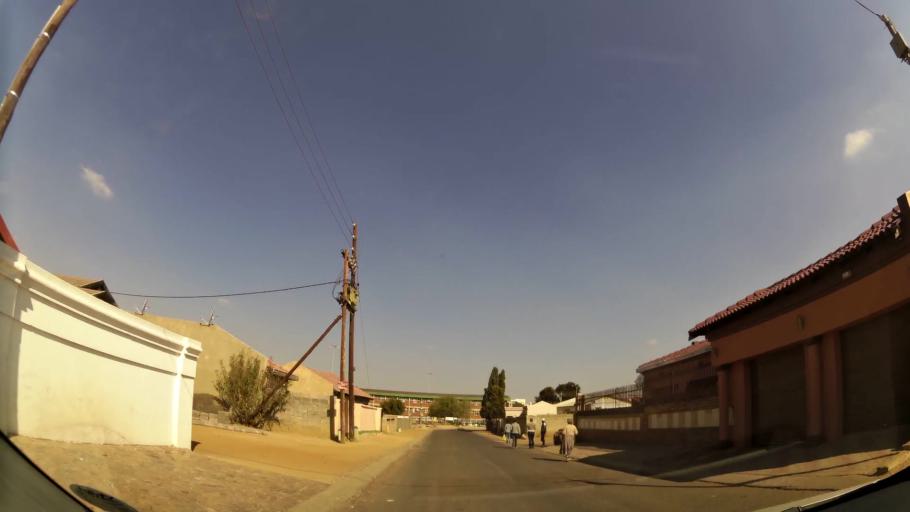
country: ZA
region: Gauteng
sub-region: City of Johannesburg Metropolitan Municipality
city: Roodepoort
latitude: -26.1637
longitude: 27.7978
